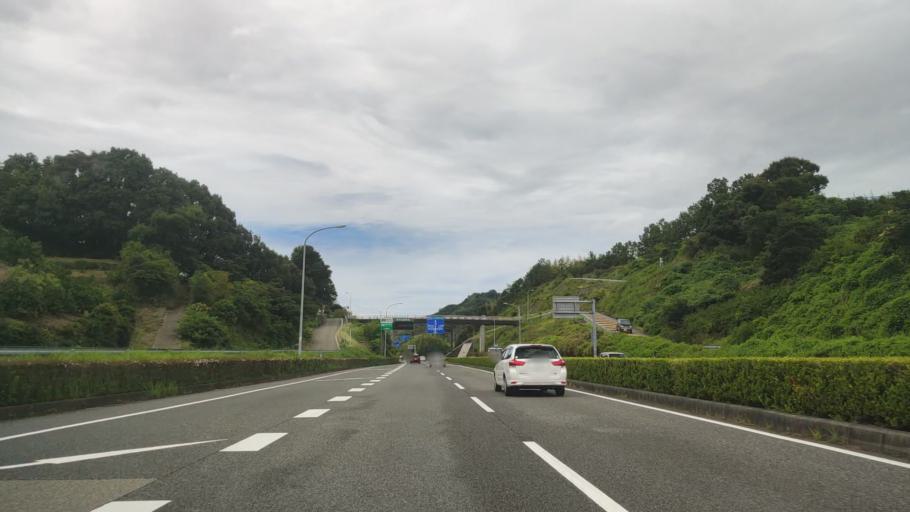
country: JP
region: Wakayama
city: Tanabe
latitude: 33.7444
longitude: 135.3831
